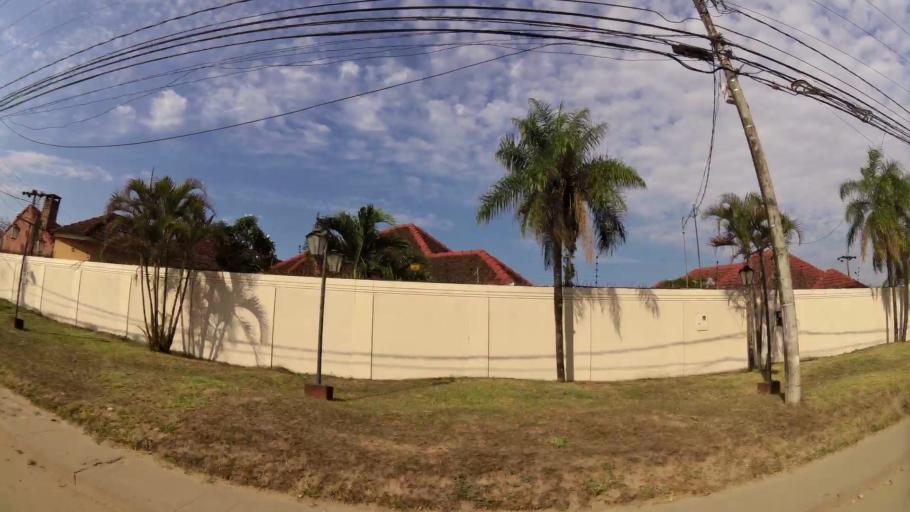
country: BO
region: Santa Cruz
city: Santa Cruz de la Sierra
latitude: -17.7229
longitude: -63.1721
